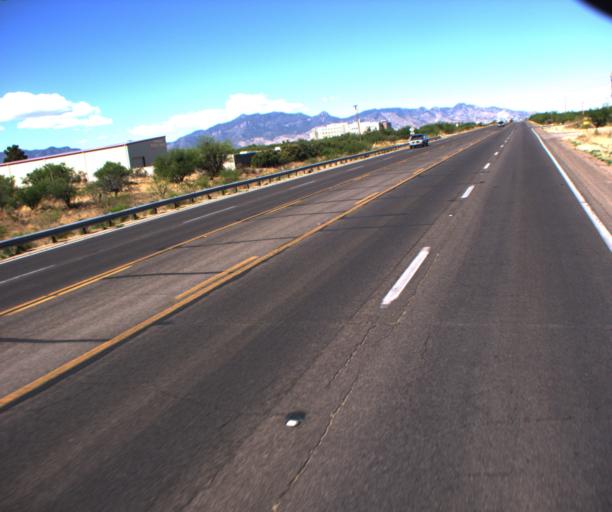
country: US
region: Arizona
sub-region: Cochise County
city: Sierra Vista
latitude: 31.5547
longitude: -110.2220
